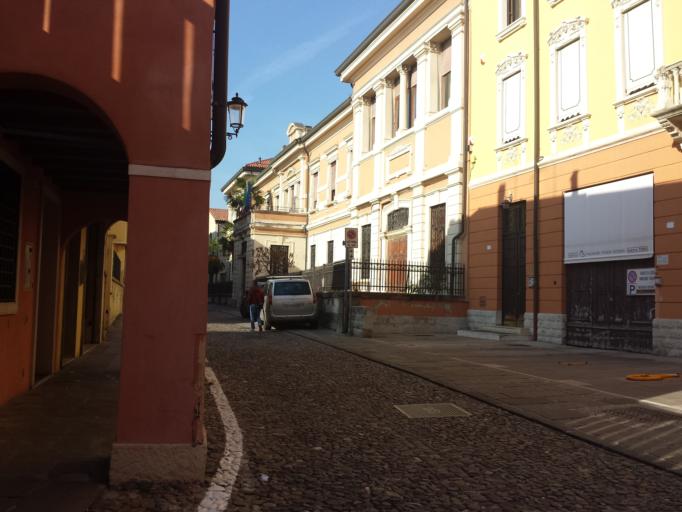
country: IT
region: Veneto
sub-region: Provincia di Padova
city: Padova
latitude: 45.4068
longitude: 11.8810
